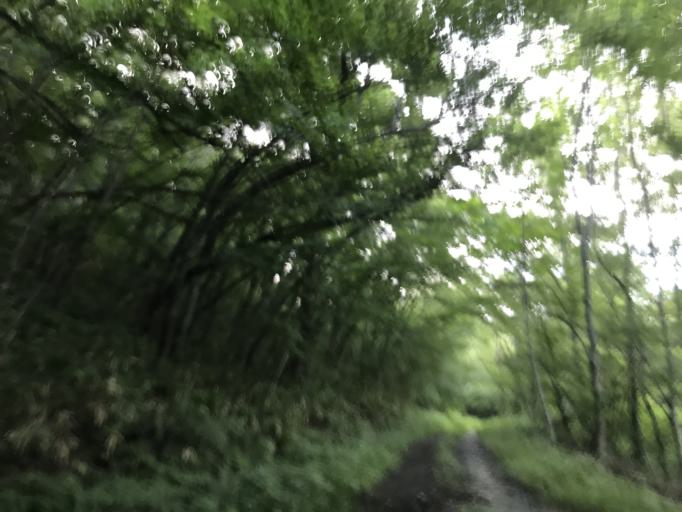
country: JP
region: Iwate
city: Ichinoseki
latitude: 38.9083
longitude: 140.9488
